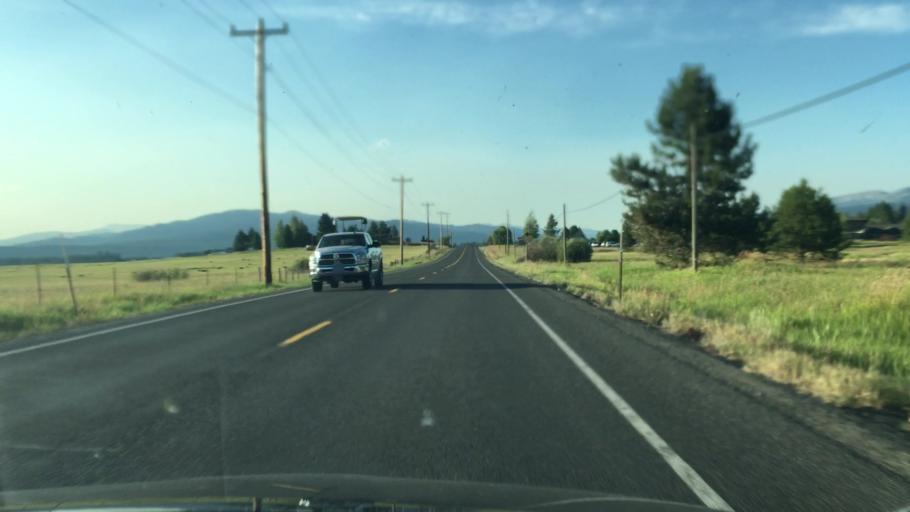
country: US
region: Idaho
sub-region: Valley County
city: McCall
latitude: 44.8769
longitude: -116.0907
